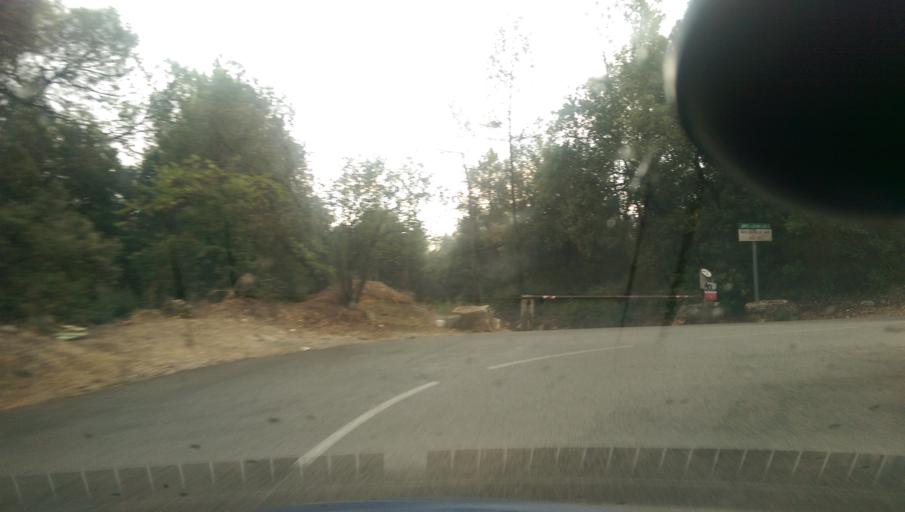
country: FR
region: Provence-Alpes-Cote d'Azur
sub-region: Departement des Alpes-Maritimes
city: Valbonne
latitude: 43.6389
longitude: 7.0412
